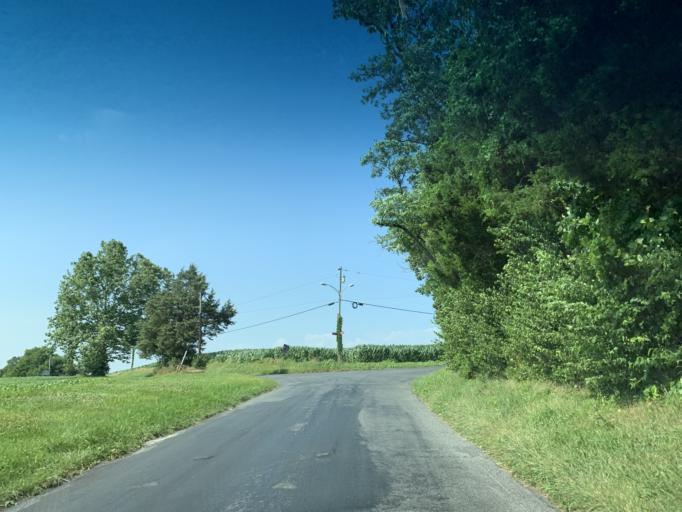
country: US
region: Maryland
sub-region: Montgomery County
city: Poolesville
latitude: 39.1323
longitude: -77.4481
